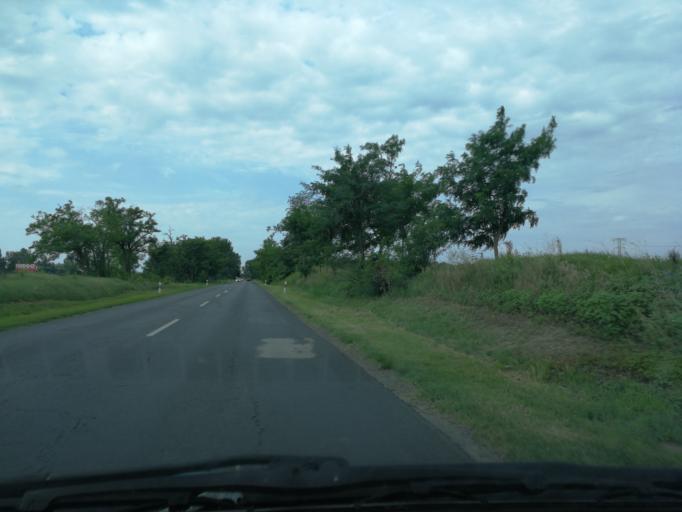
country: HU
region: Bacs-Kiskun
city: Ersekcsanad
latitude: 46.2220
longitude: 18.9658
